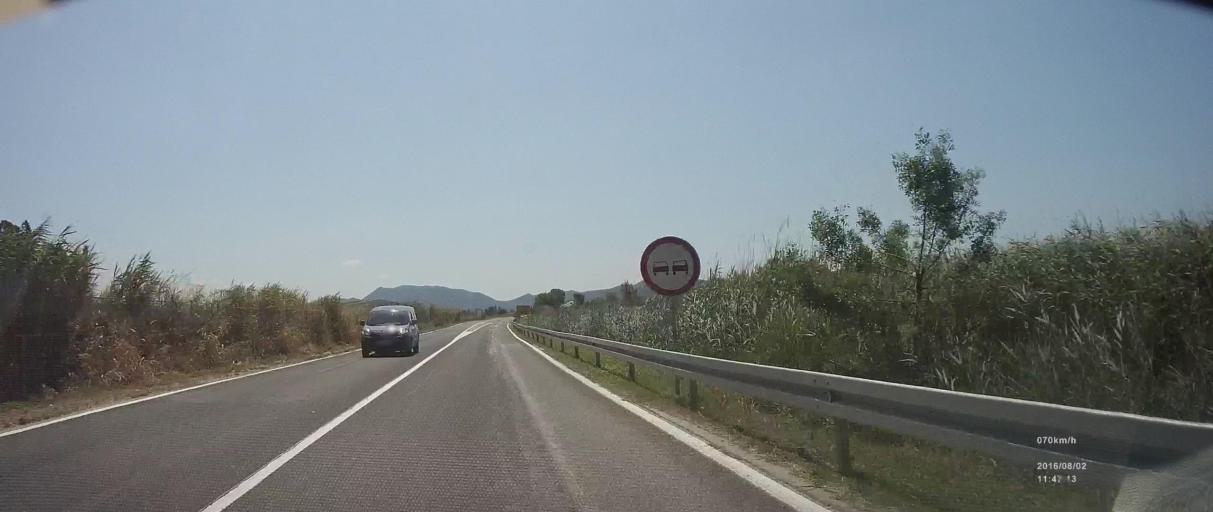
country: HR
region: Dubrovacko-Neretvanska
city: Komin
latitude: 43.0462
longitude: 17.4806
